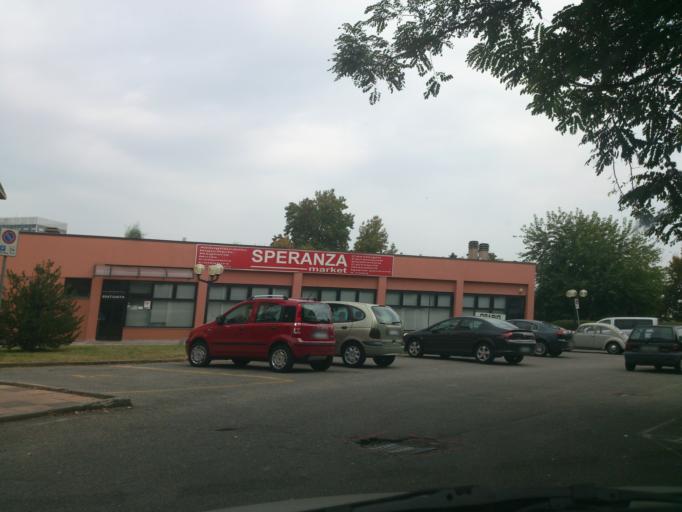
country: IT
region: Lombardy
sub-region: Citta metropolitana di Milano
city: San Donato Milanese
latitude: 45.4295
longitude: 9.2672
